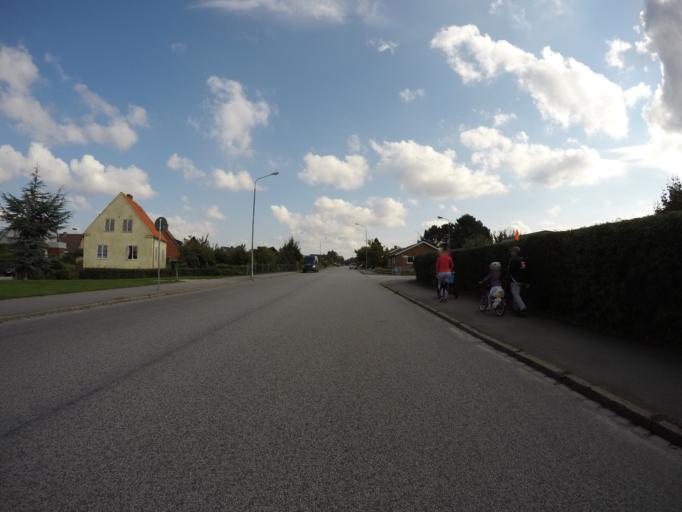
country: SE
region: Skane
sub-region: Burlovs Kommun
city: Arloev
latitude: 55.5904
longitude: 13.0737
